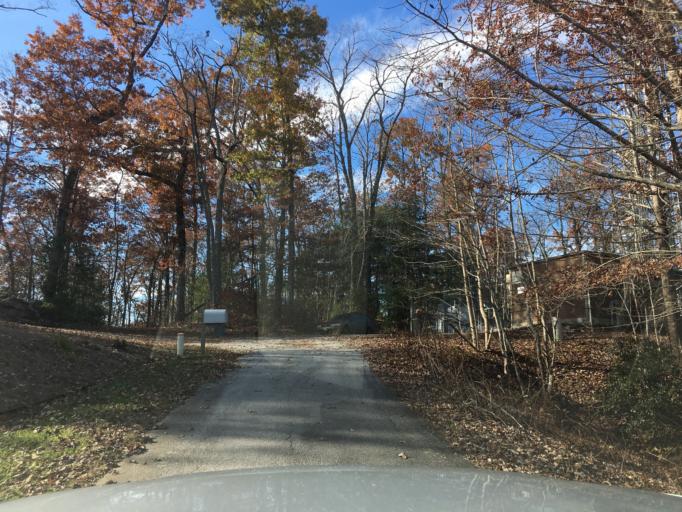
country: US
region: North Carolina
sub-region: Henderson County
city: Etowah
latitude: 35.3353
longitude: -82.6175
